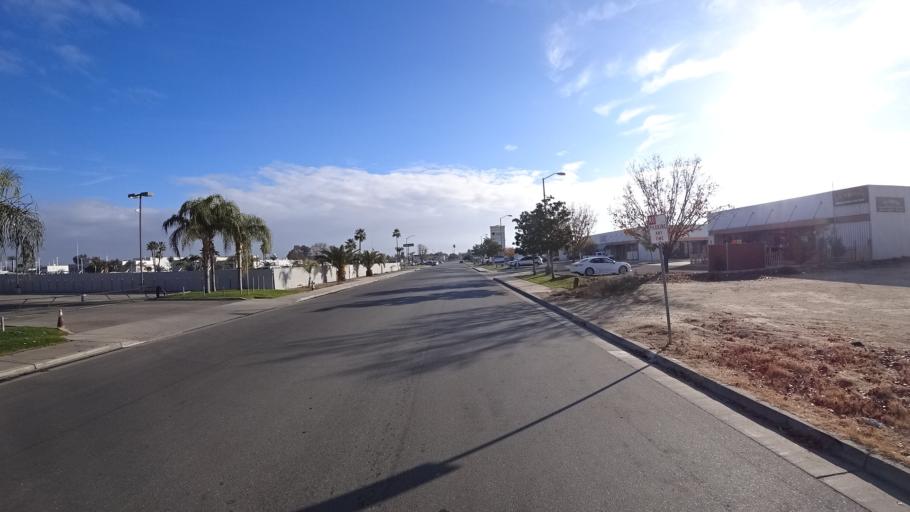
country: US
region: California
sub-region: Kern County
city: Greenfield
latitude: 35.3010
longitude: -119.0367
